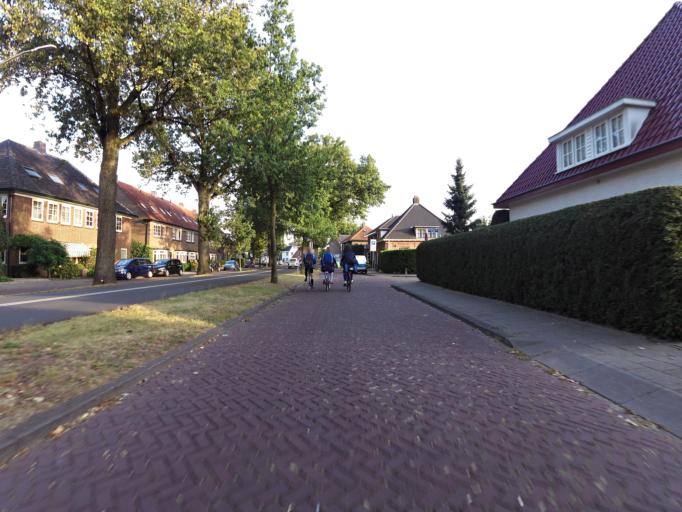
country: NL
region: Gelderland
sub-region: Gemeente Zevenaar
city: Zevenaar
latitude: 51.9304
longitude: 6.0697
